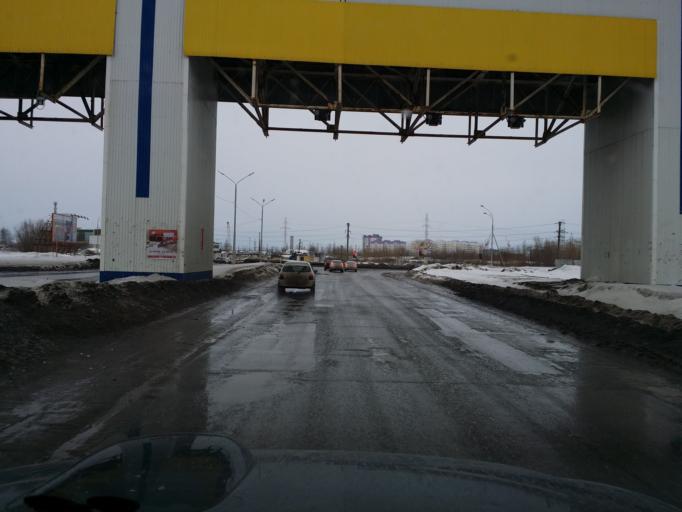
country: RU
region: Khanty-Mansiyskiy Avtonomnyy Okrug
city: Nizhnevartovsk
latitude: 60.9410
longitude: 76.6170
